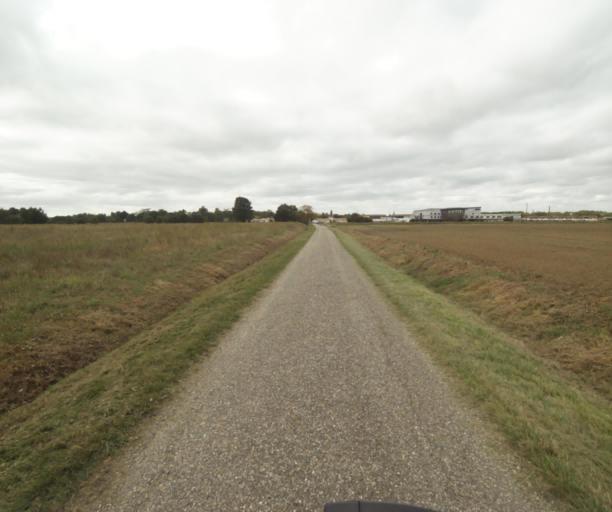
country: FR
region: Midi-Pyrenees
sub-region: Departement du Tarn-et-Garonne
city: Montech
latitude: 43.9590
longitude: 1.2574
